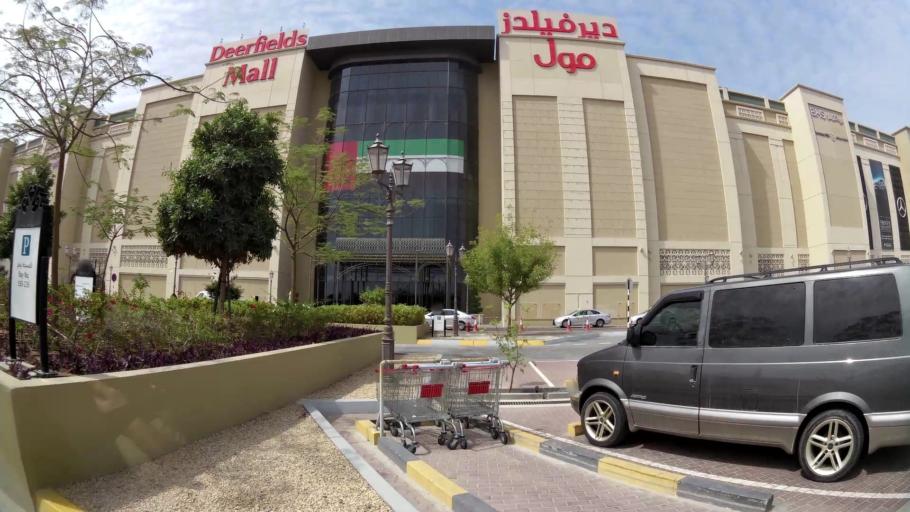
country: AE
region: Abu Dhabi
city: Abu Dhabi
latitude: 24.5231
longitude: 54.6716
